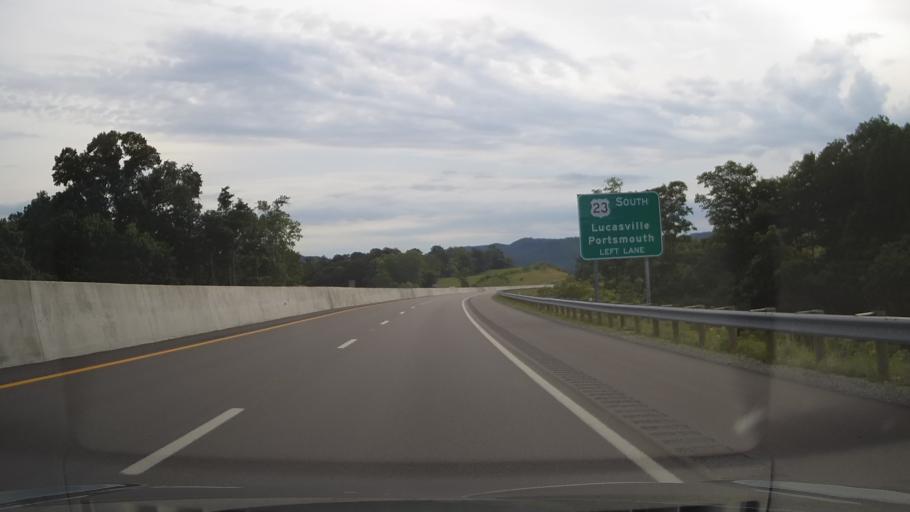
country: US
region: Ohio
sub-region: Scioto County
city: Lucasville
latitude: 38.8926
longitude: -82.9855
